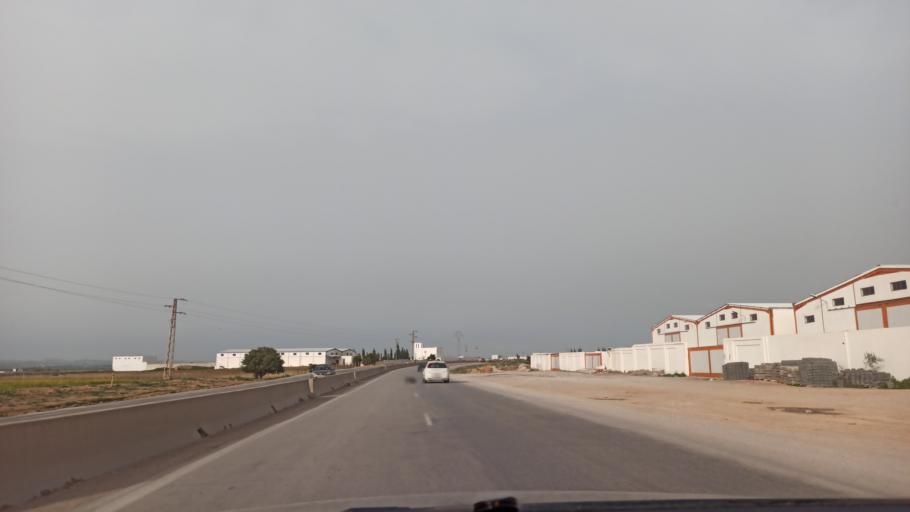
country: TN
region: Tunis
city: La Mohammedia
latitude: 36.5671
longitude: 10.0839
